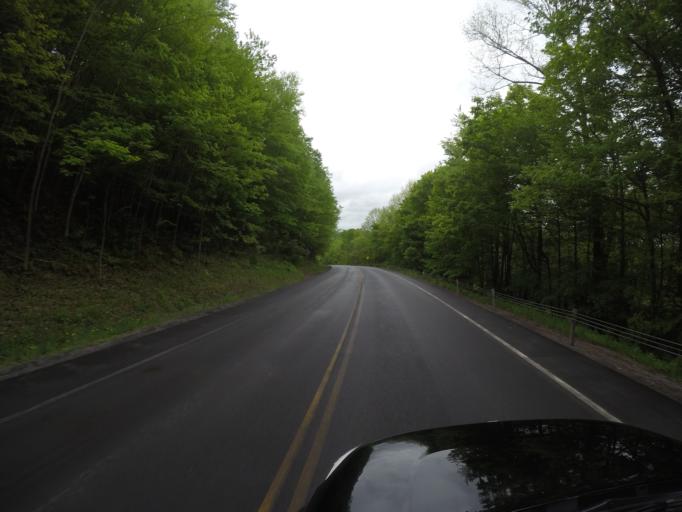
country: US
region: New York
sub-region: Delaware County
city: Delhi
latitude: 42.2394
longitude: -74.7951
